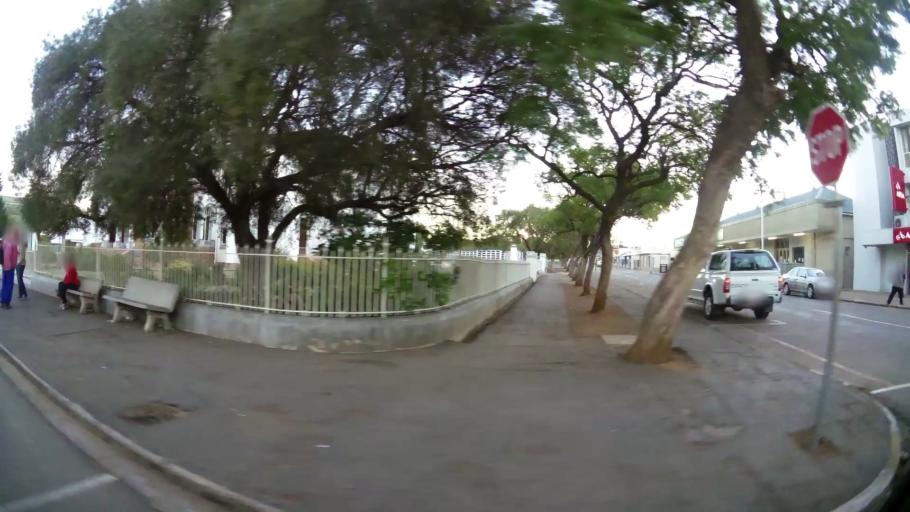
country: ZA
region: Western Cape
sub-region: Eden District Municipality
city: Riversdale
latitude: -34.0905
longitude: 21.2608
